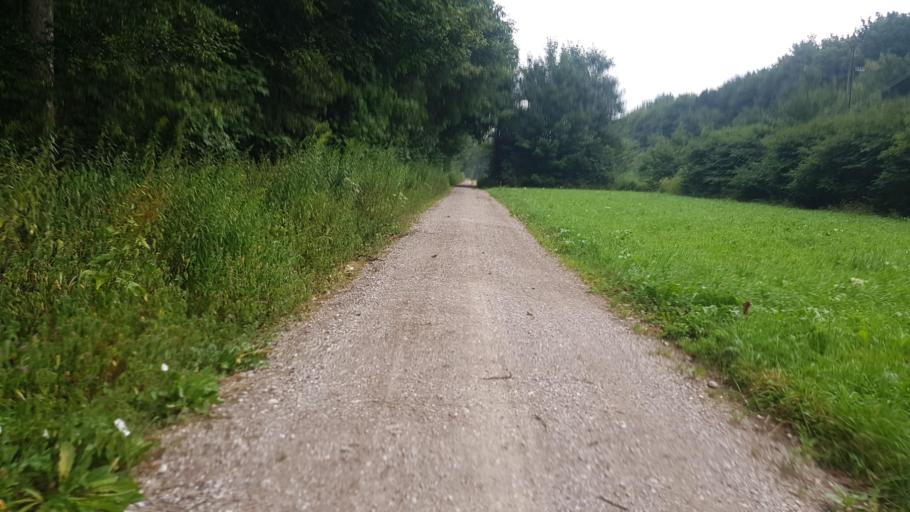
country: DE
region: Bavaria
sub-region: Upper Bavaria
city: Gauting
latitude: 48.0471
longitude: 11.3601
